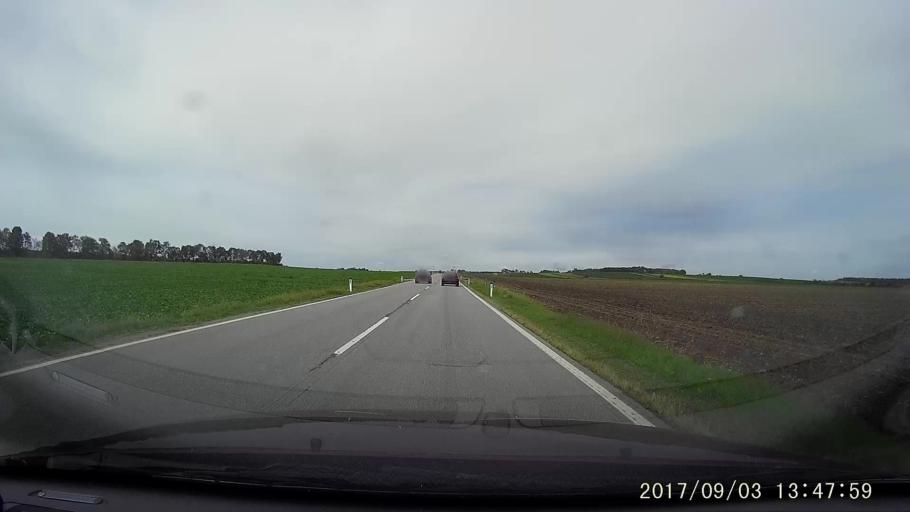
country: AT
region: Lower Austria
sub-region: Politischer Bezirk Hollabrunn
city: Guntersdorf
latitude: 48.6676
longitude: 16.0532
